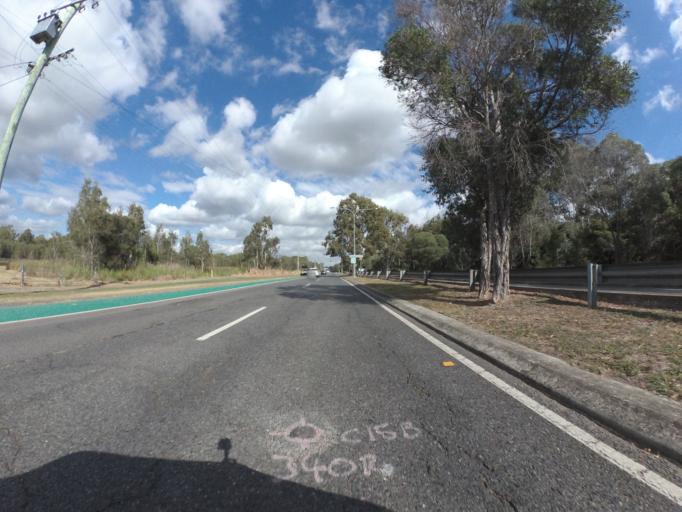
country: AU
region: Queensland
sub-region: Brisbane
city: Wynnum West
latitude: -27.4625
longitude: 153.1463
